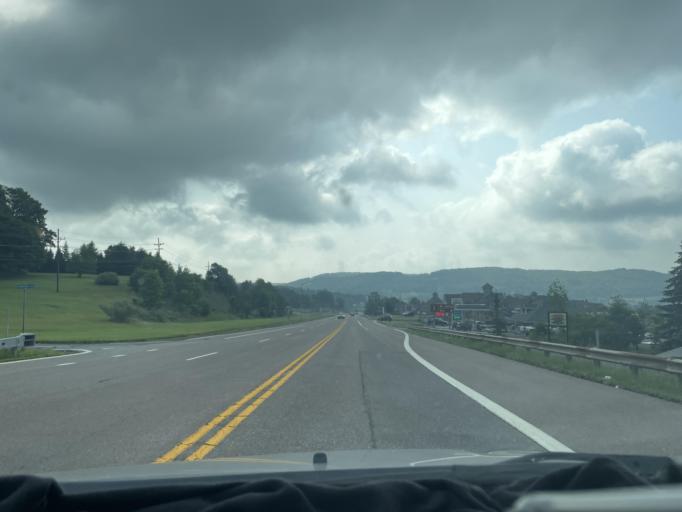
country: US
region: Maryland
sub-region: Garrett County
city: Oakland
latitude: 39.5635
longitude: -79.3614
